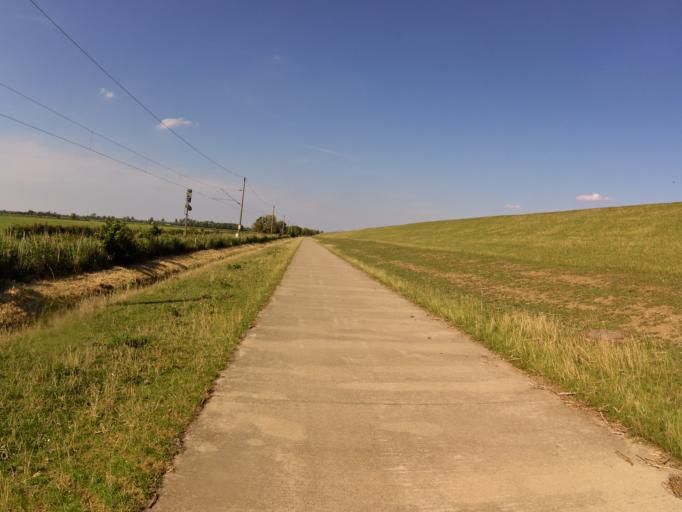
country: DE
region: Lower Saxony
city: Nordenham
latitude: 53.4497
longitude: 8.4755
